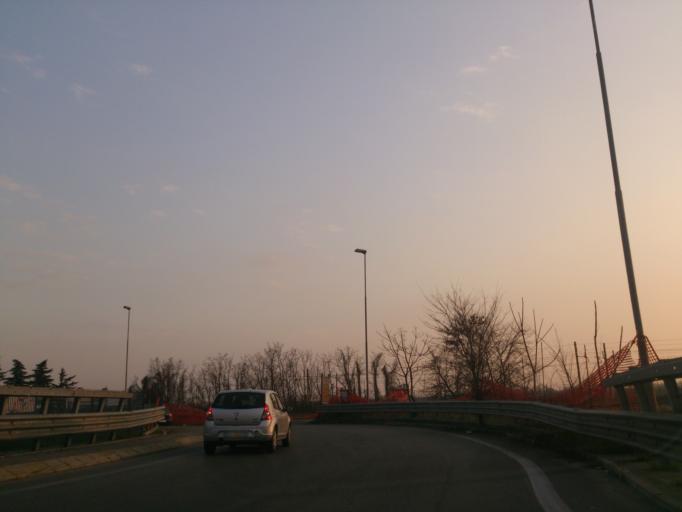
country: IT
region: Lombardy
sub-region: Citta metropolitana di Milano
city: San Giuliano Milanese
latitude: 45.3811
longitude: 9.3004
